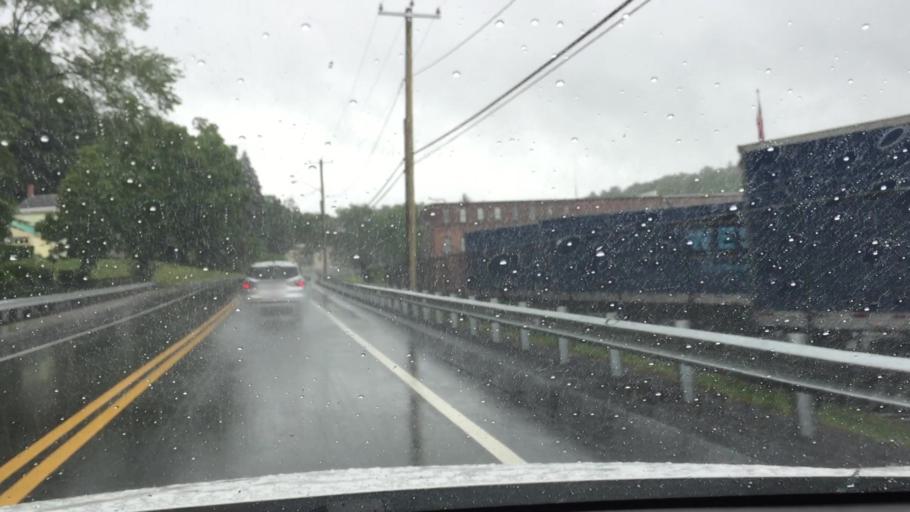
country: US
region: Massachusetts
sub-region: Berkshire County
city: Dalton
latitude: 42.4716
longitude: -73.1743
